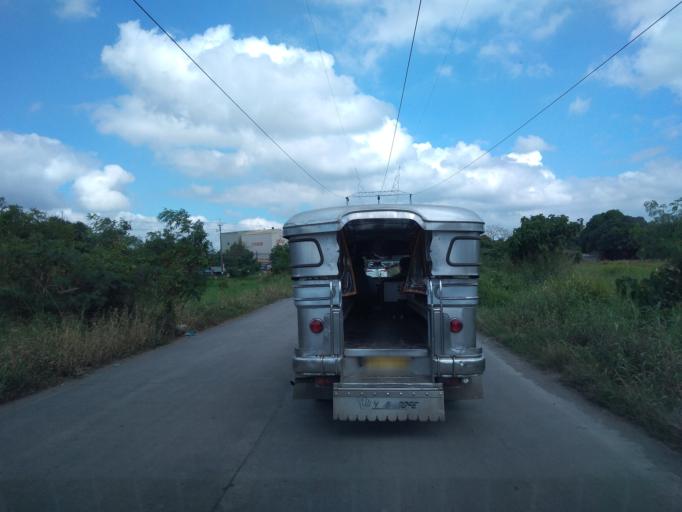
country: PH
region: Central Luzon
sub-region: Province of Bulacan
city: Santa Maria
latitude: 14.8243
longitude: 120.9700
